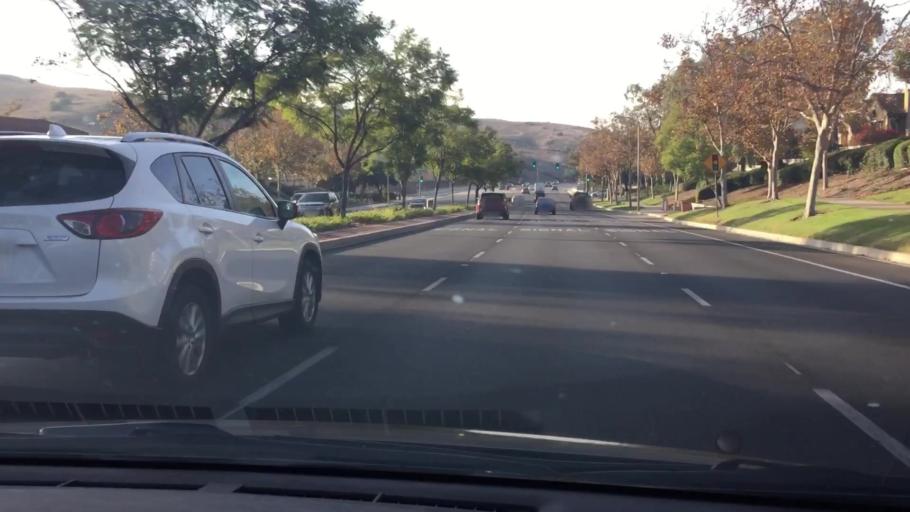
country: US
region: California
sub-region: Orange County
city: Las Flores
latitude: 33.6123
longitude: -117.6170
